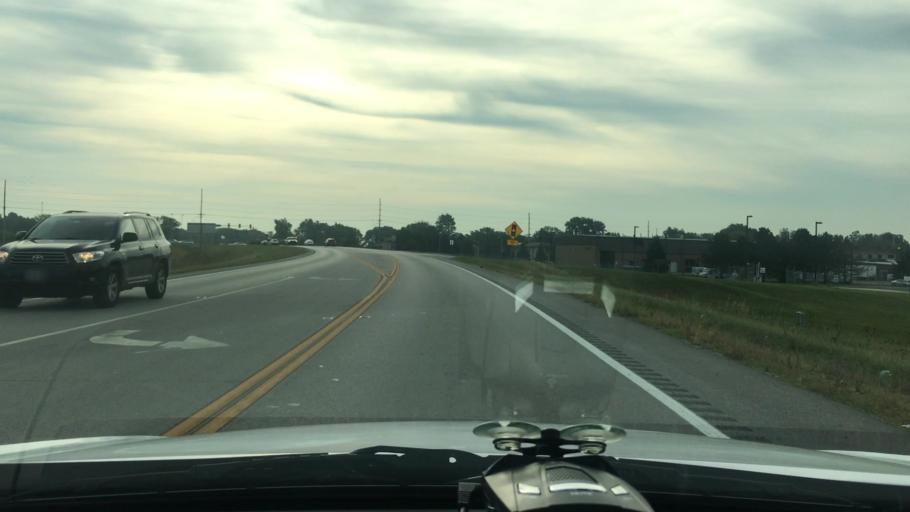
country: US
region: Illinois
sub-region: Champaign County
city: Champaign
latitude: 40.1394
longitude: -88.2809
